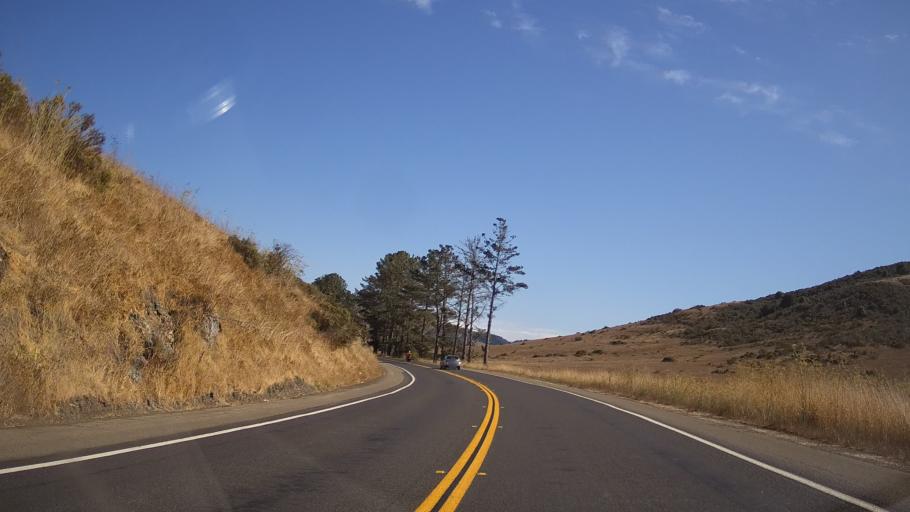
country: US
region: California
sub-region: Marin County
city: Lagunitas-Forest Knolls
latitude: 38.0828
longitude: -122.7202
